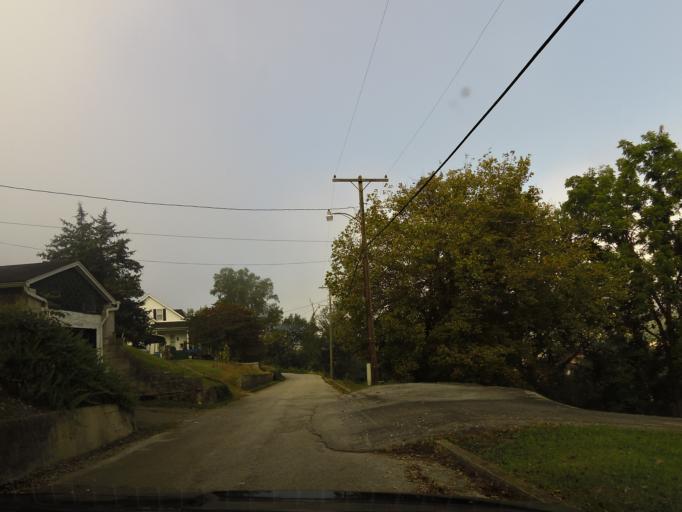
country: US
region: Tennessee
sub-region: Campbell County
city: Jellico
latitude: 36.5858
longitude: -84.1279
